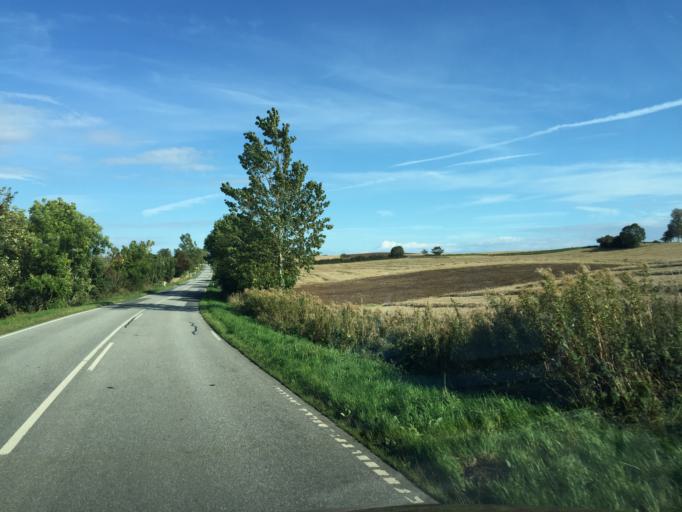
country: DK
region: South Denmark
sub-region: Sonderborg Kommune
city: Guderup
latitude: 55.0006
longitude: 9.9193
